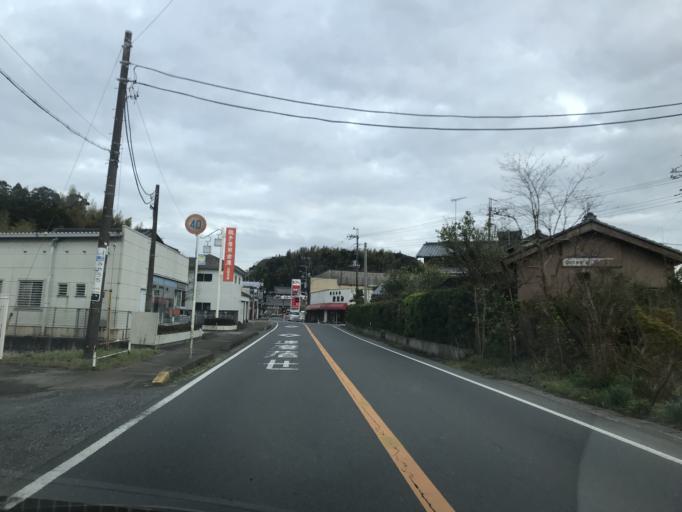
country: JP
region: Chiba
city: Omigawa
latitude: 35.8032
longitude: 140.6032
